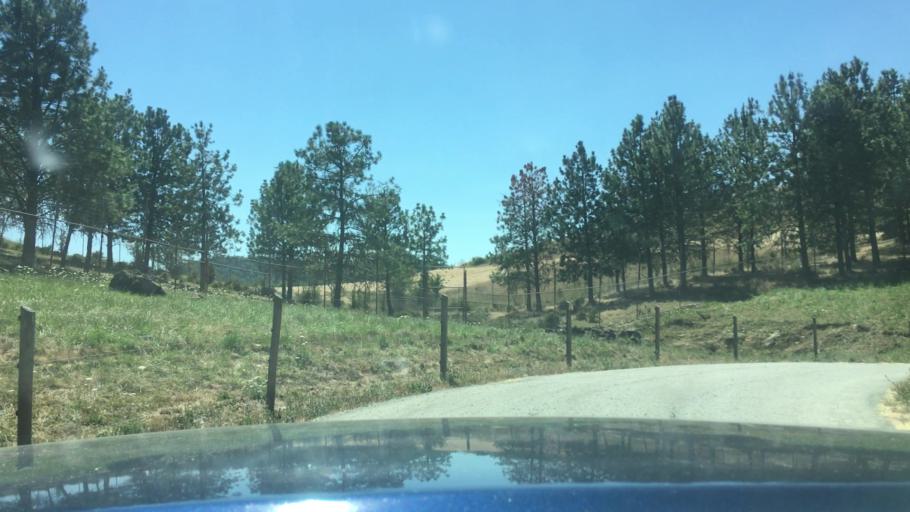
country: US
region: Oregon
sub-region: Douglas County
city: Winston
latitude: 43.1321
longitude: -123.4377
